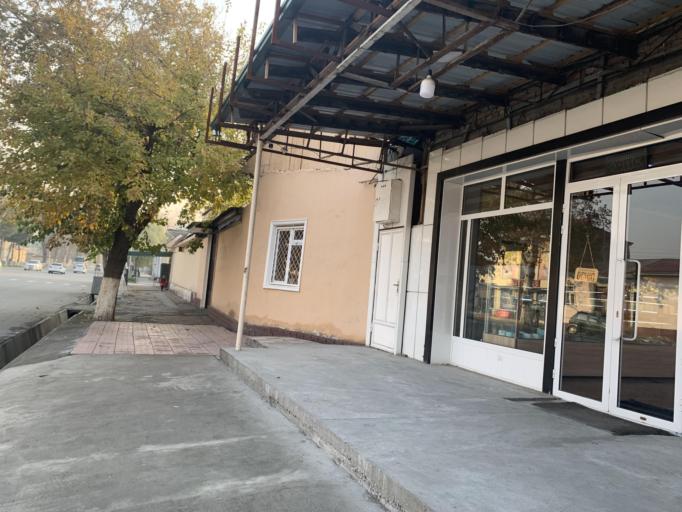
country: UZ
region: Fergana
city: Qo`qon
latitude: 40.5342
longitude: 70.9375
